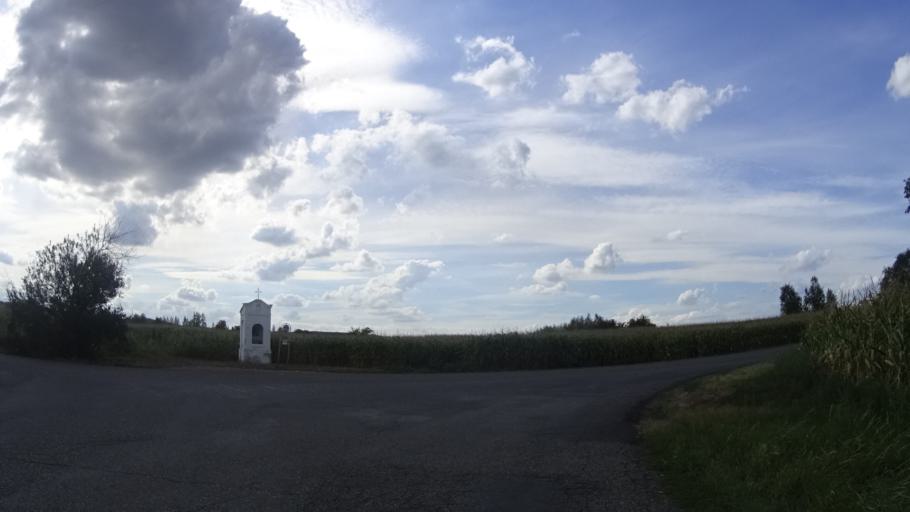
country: CZ
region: Olomoucky
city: Bila Lhota
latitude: 49.7300
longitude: 16.9807
